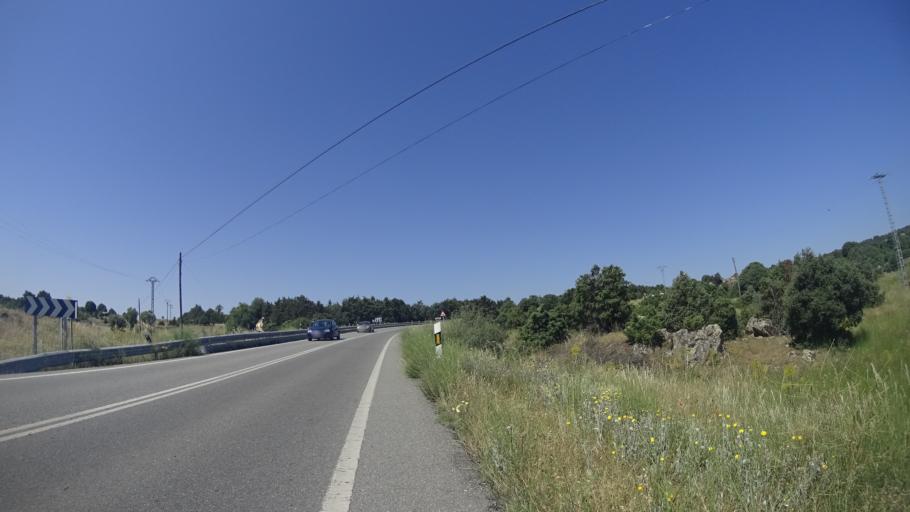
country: ES
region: Madrid
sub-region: Provincia de Madrid
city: Hoyo de Manzanares
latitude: 40.6016
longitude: -3.9125
